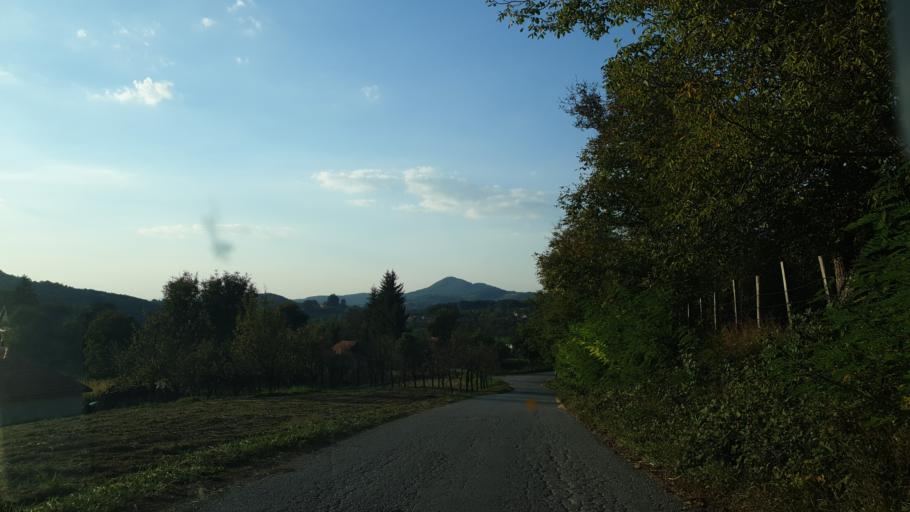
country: RS
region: Central Serbia
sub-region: Zlatiborski Okrug
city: Pozega
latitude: 43.9684
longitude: 20.0238
